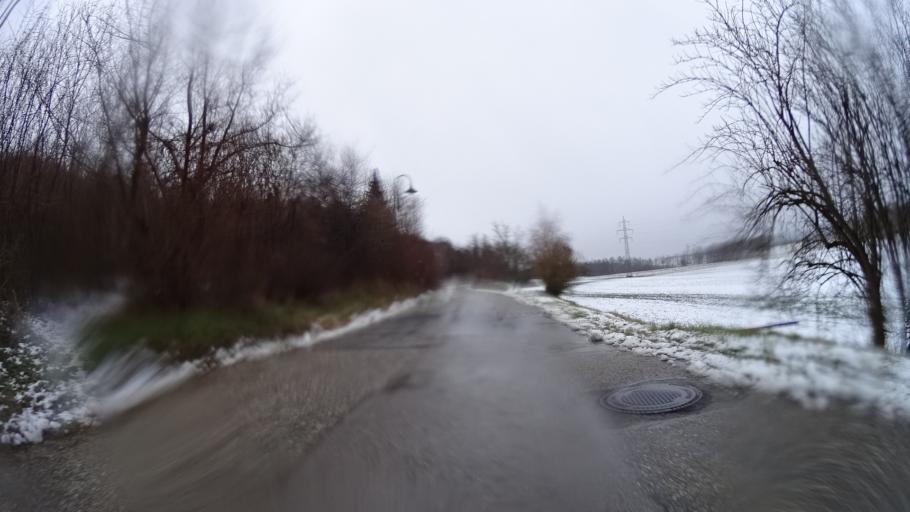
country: AT
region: Lower Austria
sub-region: Politischer Bezirk Korneuburg
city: Leobendorf
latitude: 48.3748
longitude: 16.2964
